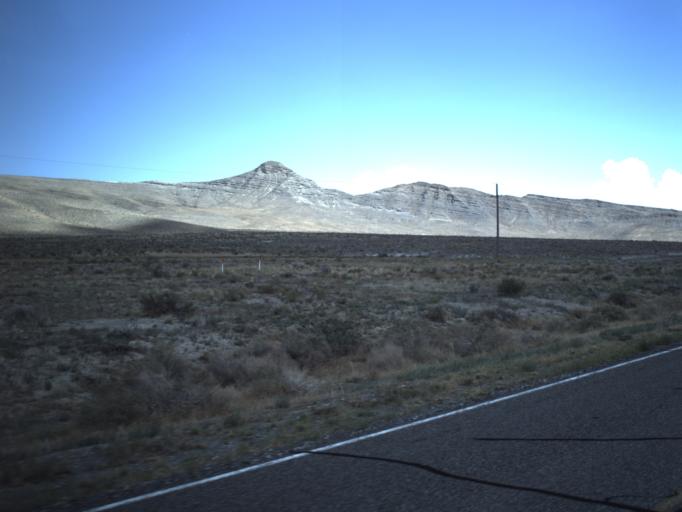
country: US
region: Utah
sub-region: Beaver County
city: Milford
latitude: 39.0443
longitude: -113.4077
